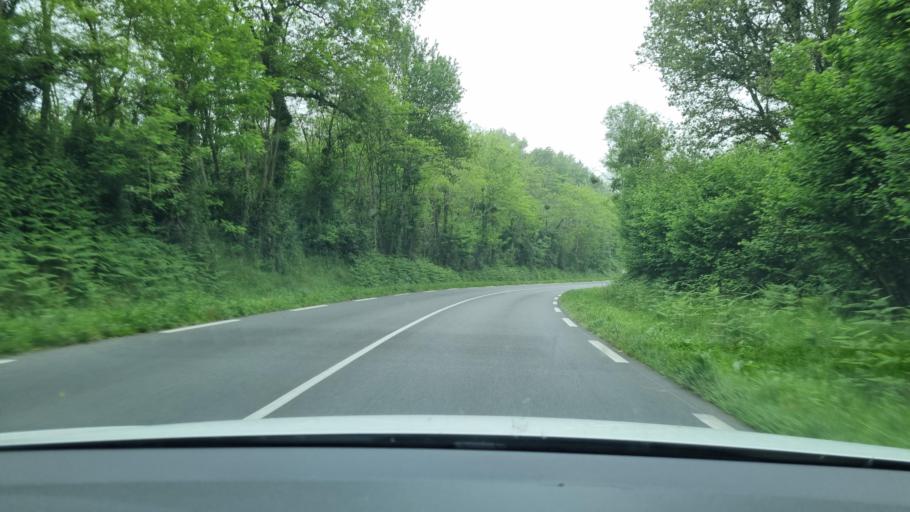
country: FR
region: Aquitaine
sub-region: Departement des Landes
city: Hagetmau
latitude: 43.5951
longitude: -0.6488
